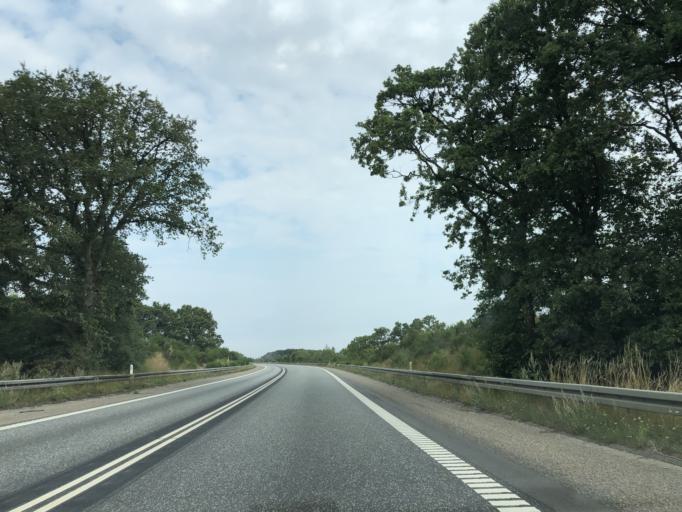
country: DK
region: Central Jutland
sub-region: Silkeborg Kommune
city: Kjellerup
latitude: 56.3507
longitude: 9.5300
